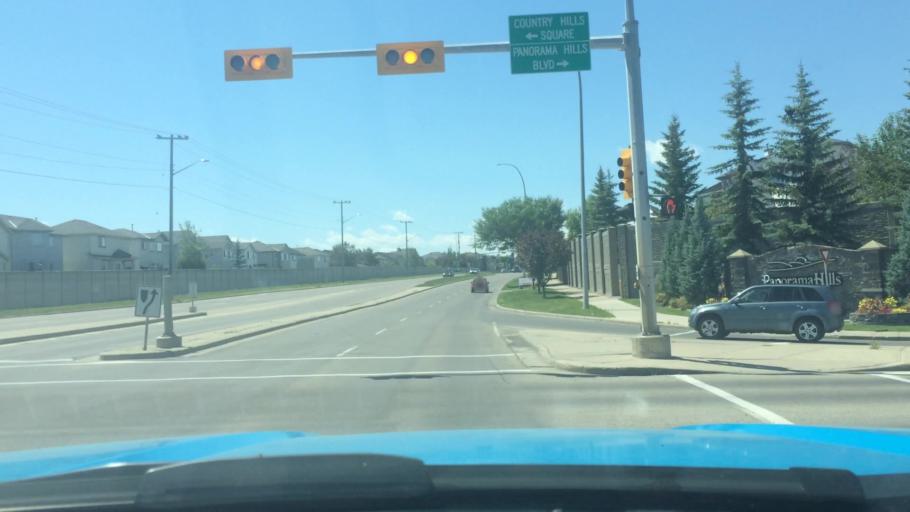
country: CA
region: Alberta
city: Calgary
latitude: 51.1487
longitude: -114.0737
